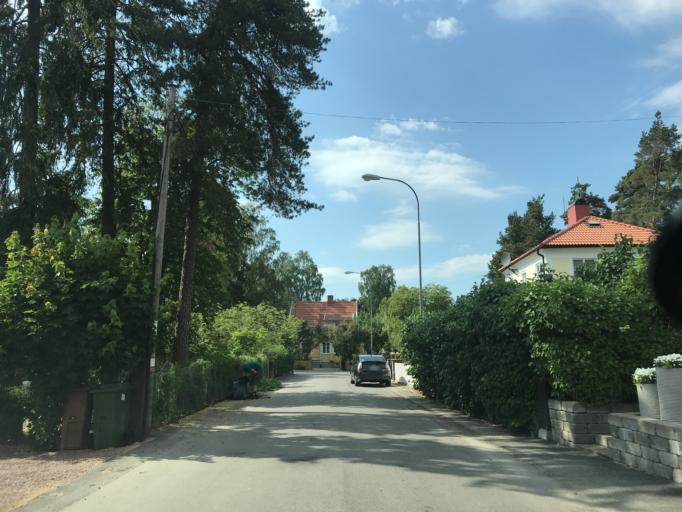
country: SE
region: Stockholm
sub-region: Stockholms Kommun
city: Kista
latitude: 59.4079
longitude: 17.9715
